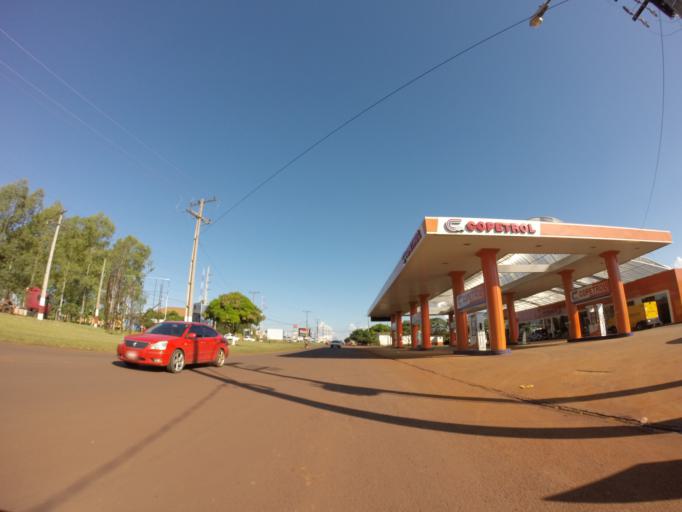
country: PY
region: Alto Parana
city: Ciudad del Este
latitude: -25.3882
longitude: -54.6419
